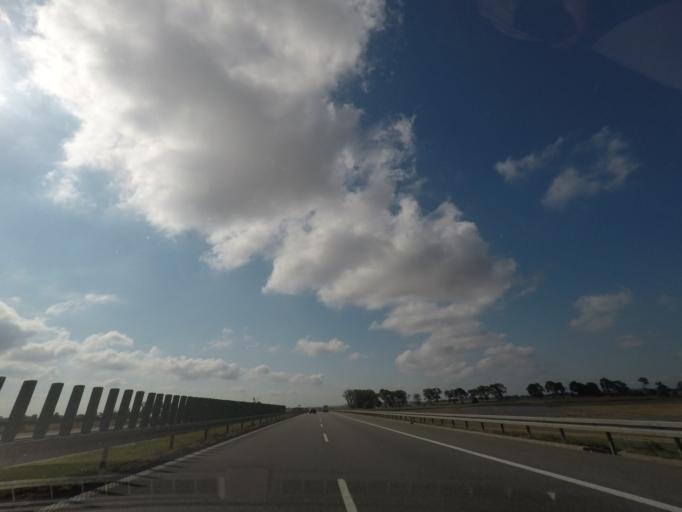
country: PL
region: Pomeranian Voivodeship
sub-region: Powiat gdanski
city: Pszczolki
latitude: 54.1385
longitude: 18.6746
